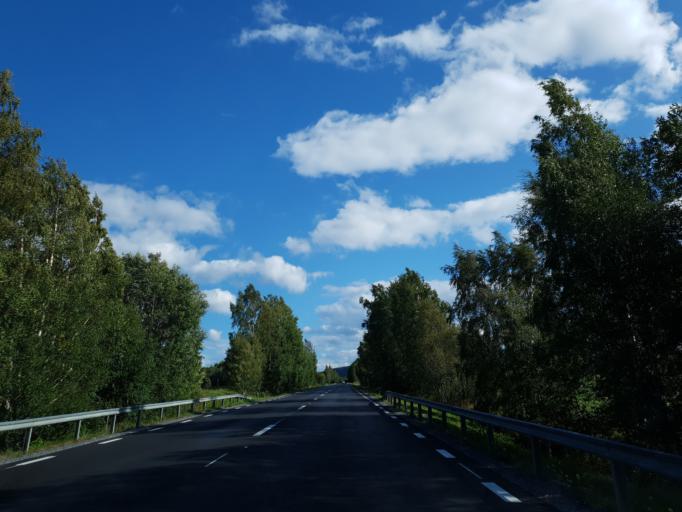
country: SE
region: Vaesternorrland
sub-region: OErnskoeldsviks Kommun
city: Bjasta
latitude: 63.1806
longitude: 18.5311
